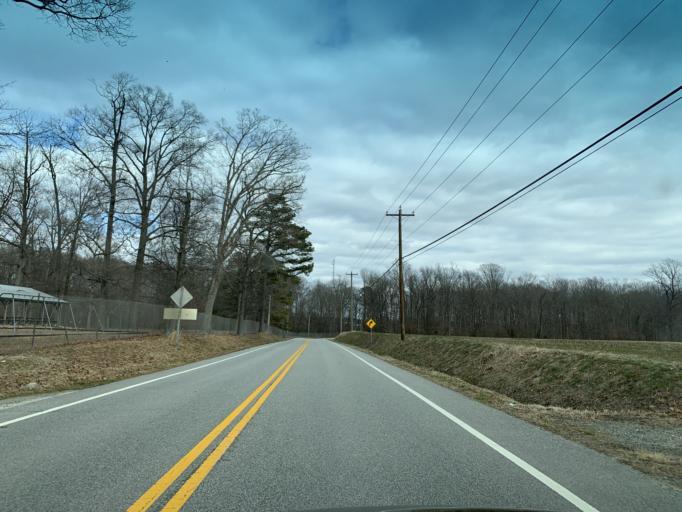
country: US
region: Maryland
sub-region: Queen Anne's County
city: Centreville
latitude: 39.0276
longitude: -76.1172
